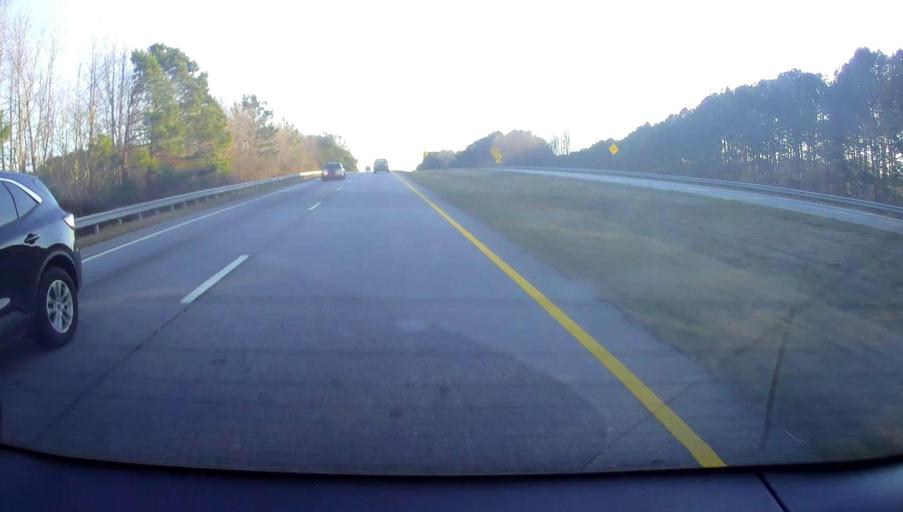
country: US
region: Georgia
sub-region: Fayette County
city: Tyrone
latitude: 33.4851
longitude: -84.5853
